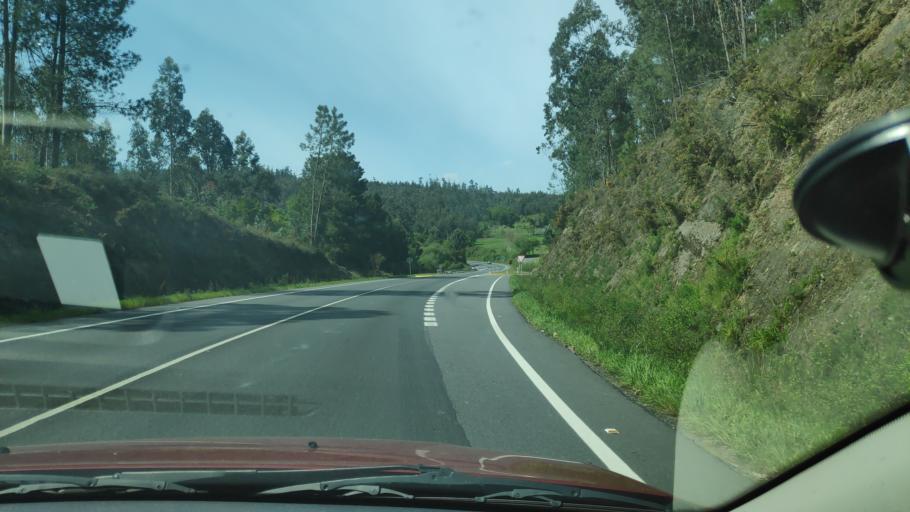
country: ES
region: Galicia
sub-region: Provincia da Coruna
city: Ames
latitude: 42.8766
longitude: -8.6619
